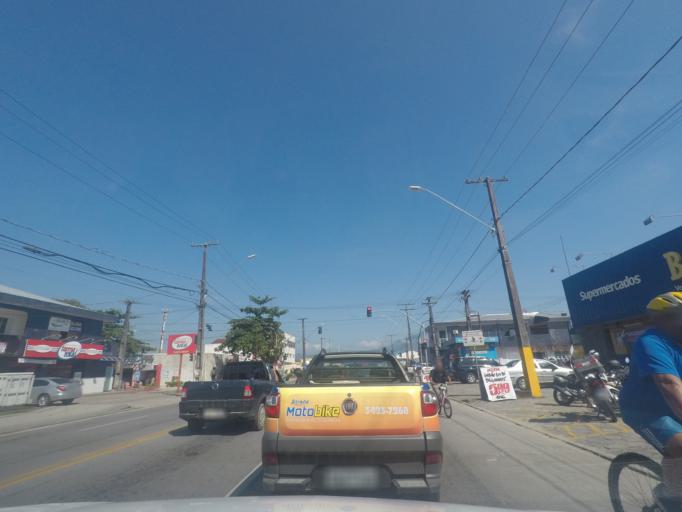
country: BR
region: Parana
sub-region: Paranagua
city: Paranagua
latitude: -25.5574
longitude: -48.5574
